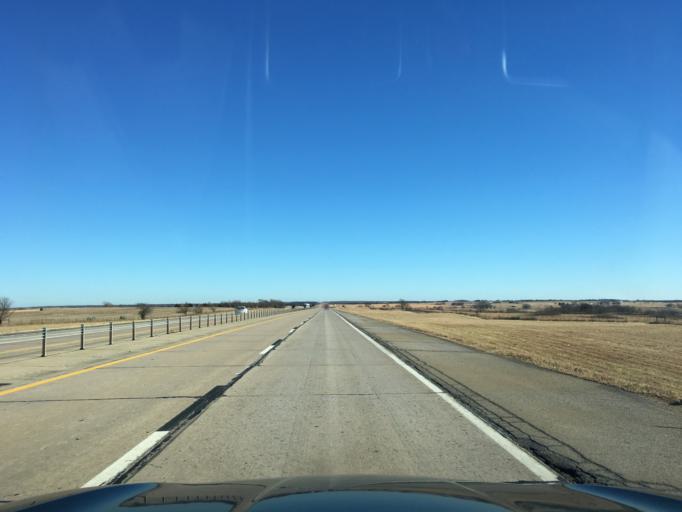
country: US
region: Oklahoma
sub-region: Pawnee County
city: Pawnee
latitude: 36.2254
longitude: -96.8717
